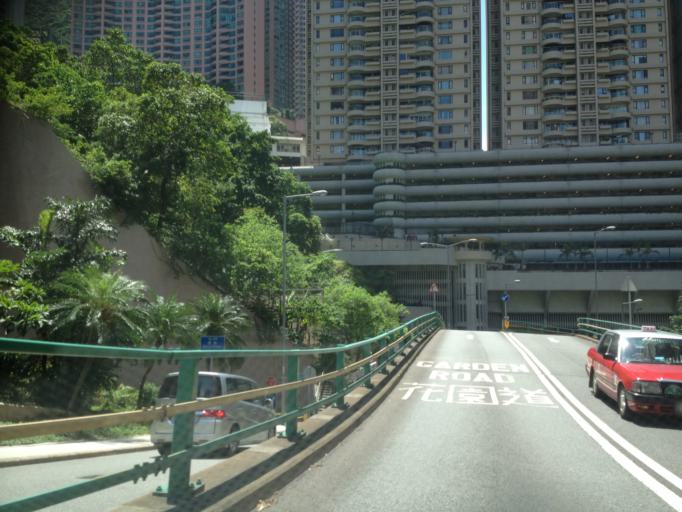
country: HK
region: Central and Western
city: Central
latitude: 22.2752
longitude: 114.1555
